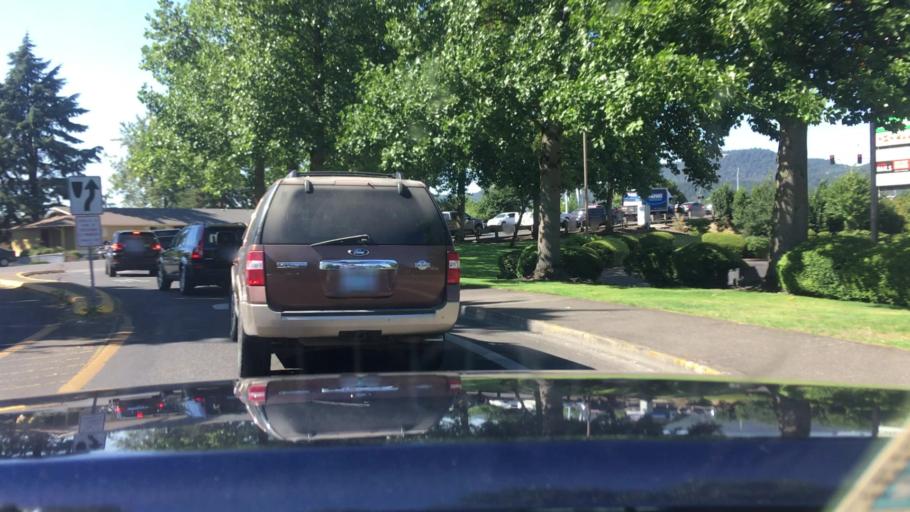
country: US
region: Oregon
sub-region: Lane County
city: Springfield
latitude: 44.0605
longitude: -122.9982
